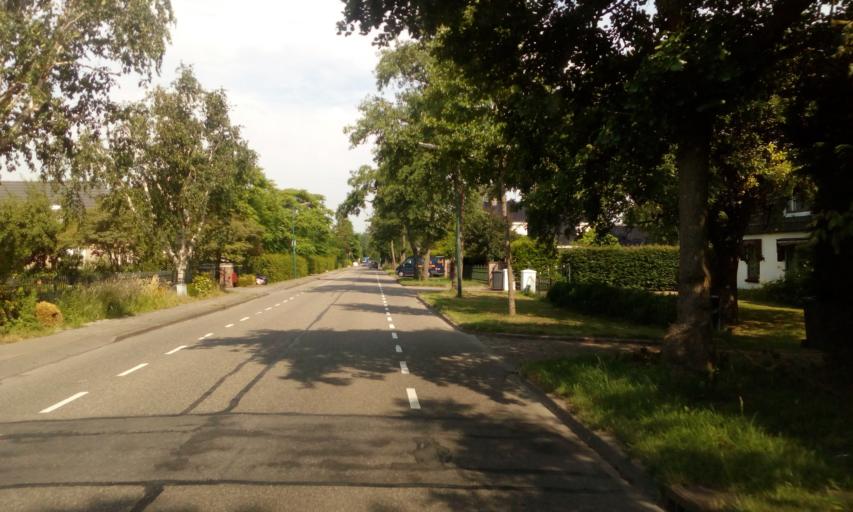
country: NL
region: Utrecht
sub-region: Stichtse Vecht
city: Maarssen
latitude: 52.1451
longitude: 5.0656
